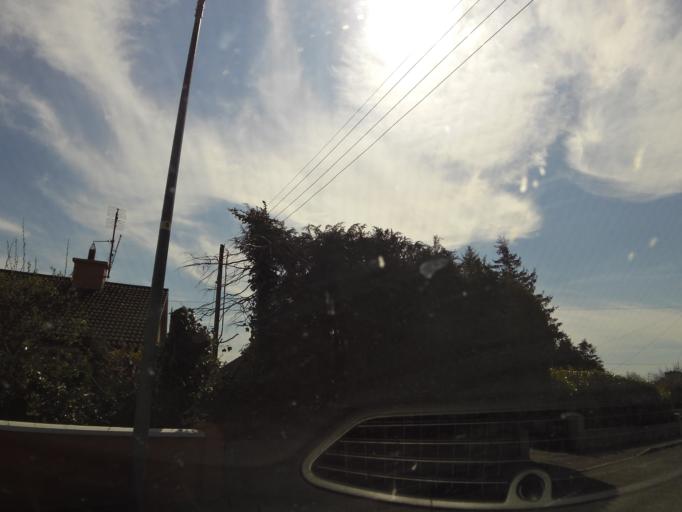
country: IE
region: Connaught
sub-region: Maigh Eo
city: Kiltamagh
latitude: 53.8463
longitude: -9.0013
